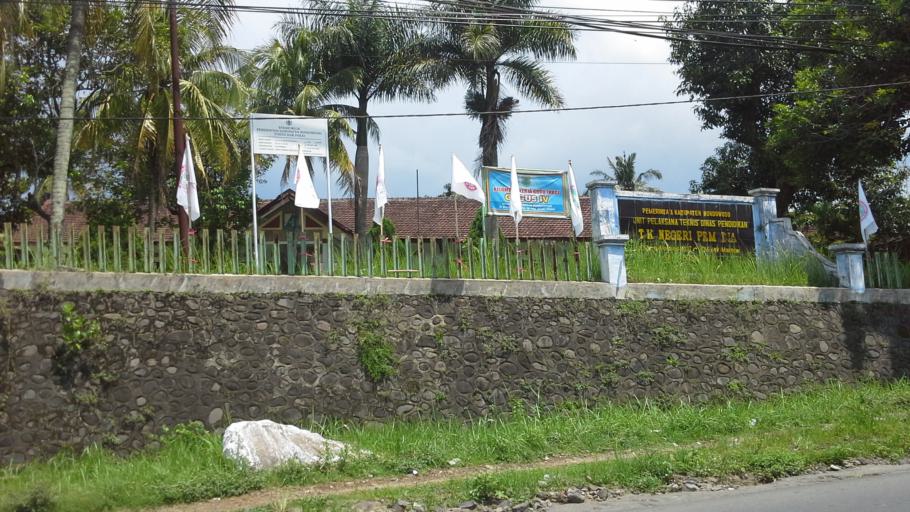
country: ID
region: East Java
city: Maesan
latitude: -8.0261
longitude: 113.7769
